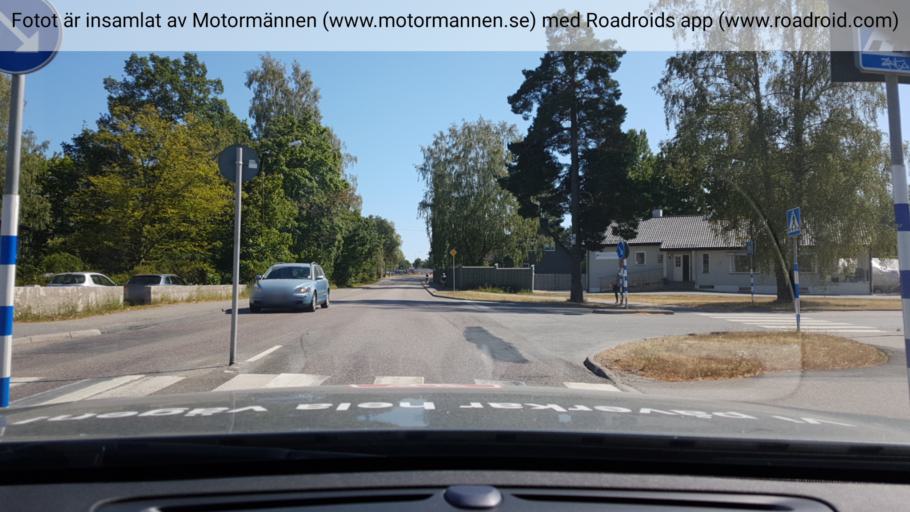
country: SE
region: Stockholm
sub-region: Haninge Kommun
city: Haninge
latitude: 59.1735
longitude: 18.1460
